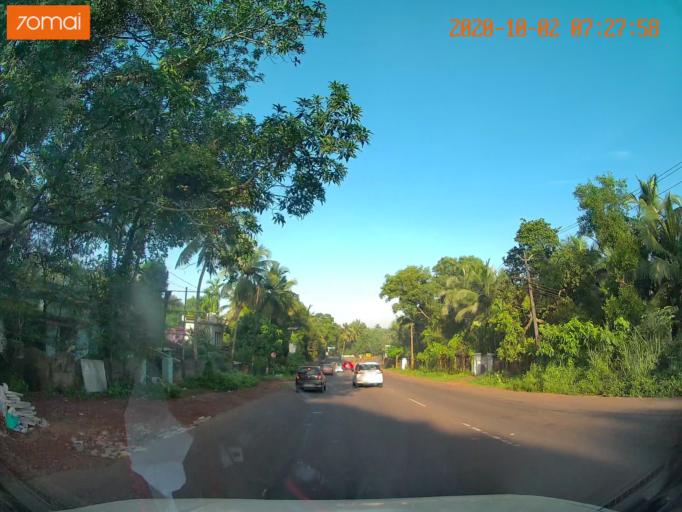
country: IN
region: Kerala
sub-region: Malappuram
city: Pariyapuram
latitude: 11.0273
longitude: 75.9457
